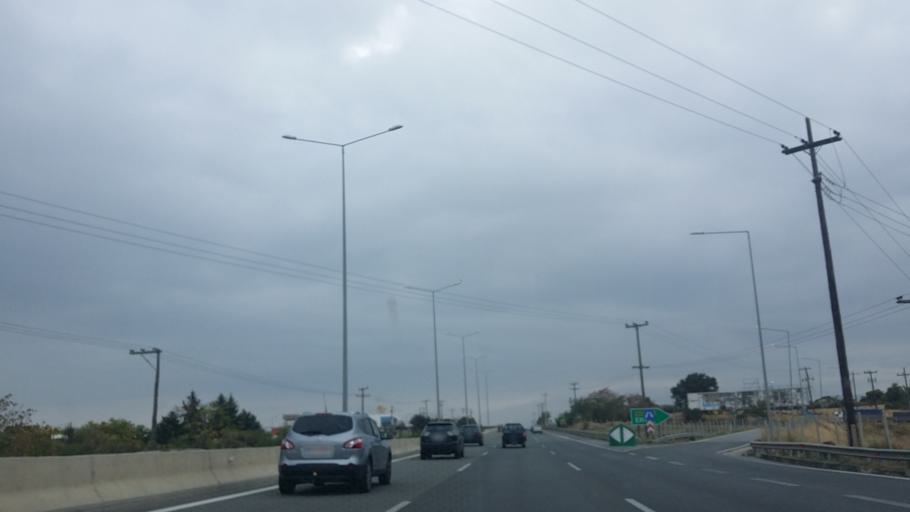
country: GR
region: Central Greece
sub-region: Nomos Voiotias
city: Oinofyta
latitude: 38.3273
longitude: 23.6090
